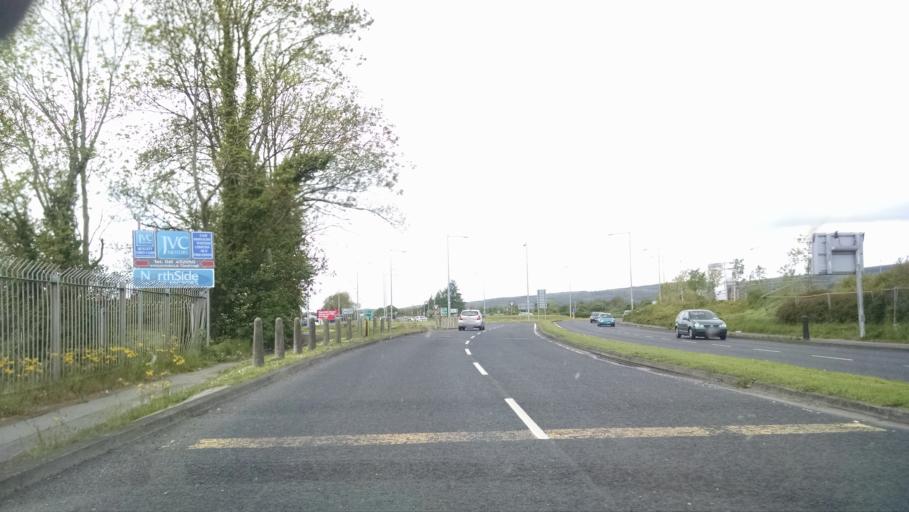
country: IE
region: Munster
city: Moyross
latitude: 52.6757
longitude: -8.6803
